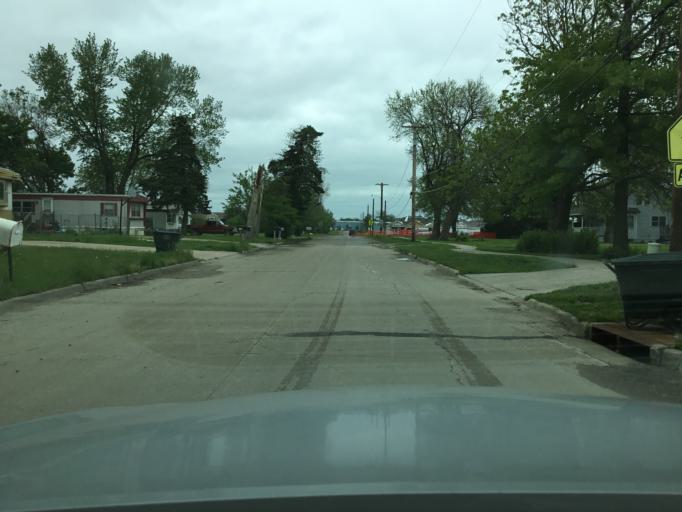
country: US
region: Kansas
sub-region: Franklin County
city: Ottawa
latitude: 38.6336
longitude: -95.2586
